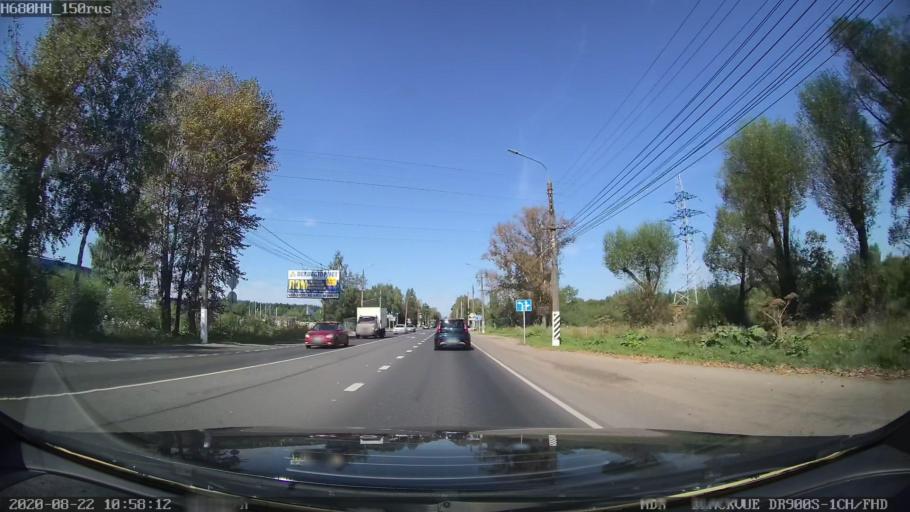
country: RU
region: Tverskaya
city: Tver
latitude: 56.8166
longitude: 35.9869
